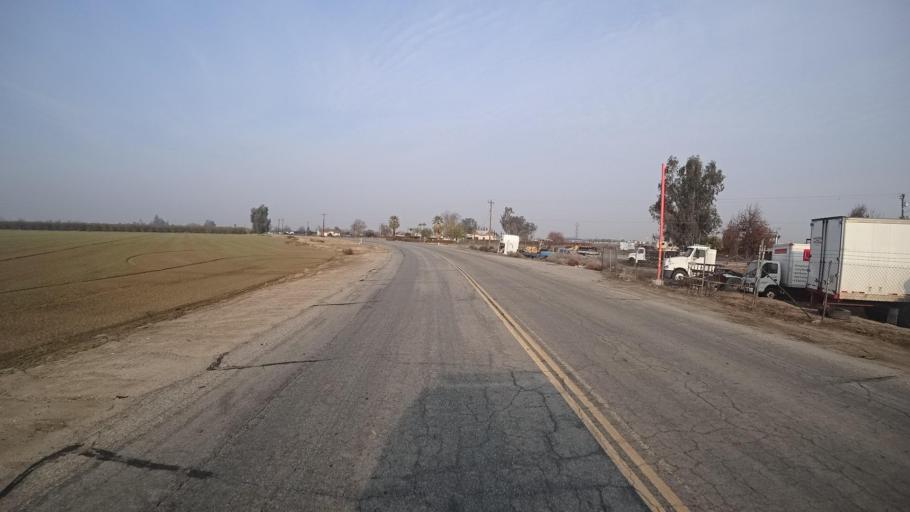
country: US
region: California
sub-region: Kern County
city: Greenfield
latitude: 35.2590
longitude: -119.0226
